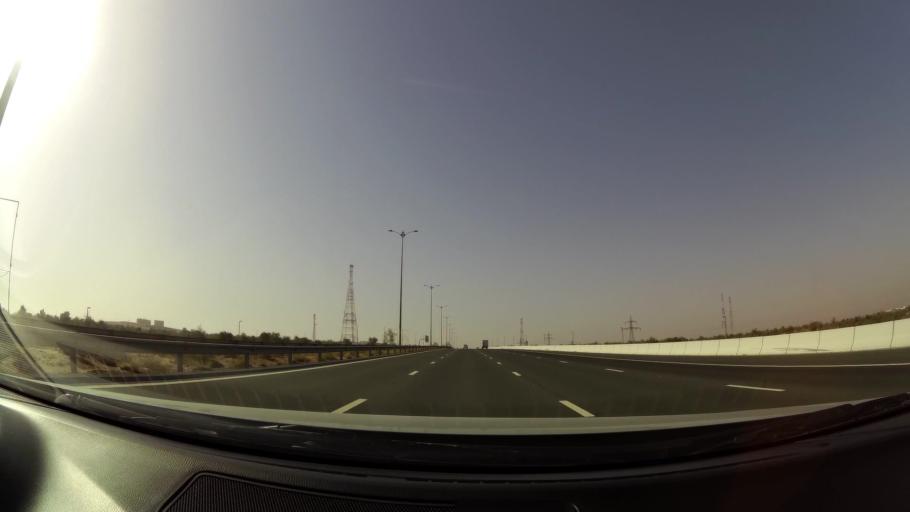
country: OM
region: Al Buraimi
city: Al Buraymi
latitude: 24.5832
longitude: 55.7417
